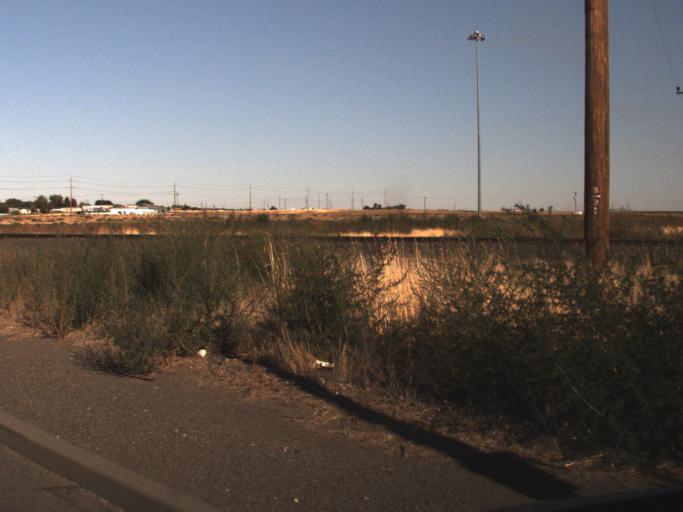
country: US
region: Washington
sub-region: Franklin County
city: Pasco
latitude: 46.2226
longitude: -119.0775
